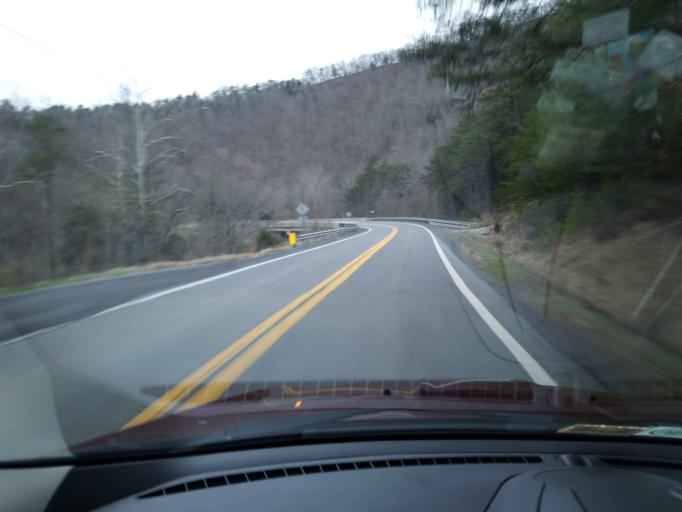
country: US
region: West Virginia
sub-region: Monroe County
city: Union
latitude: 37.5247
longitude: -80.6140
